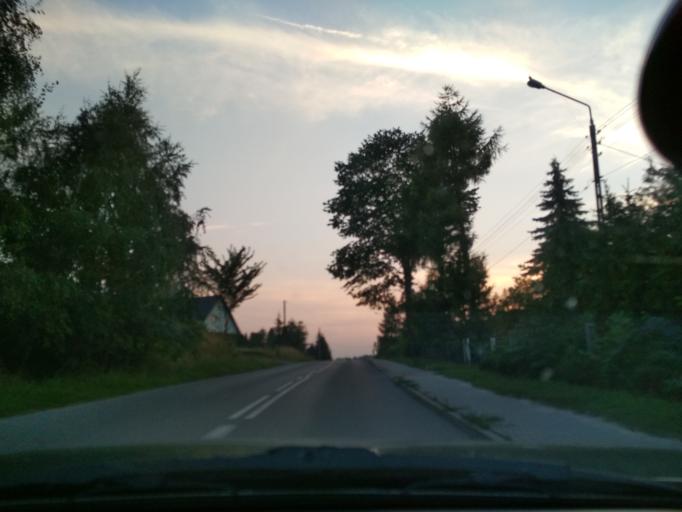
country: PL
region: Silesian Voivodeship
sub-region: Powiat zawiercianski
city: Pilica
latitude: 50.4665
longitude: 19.7076
